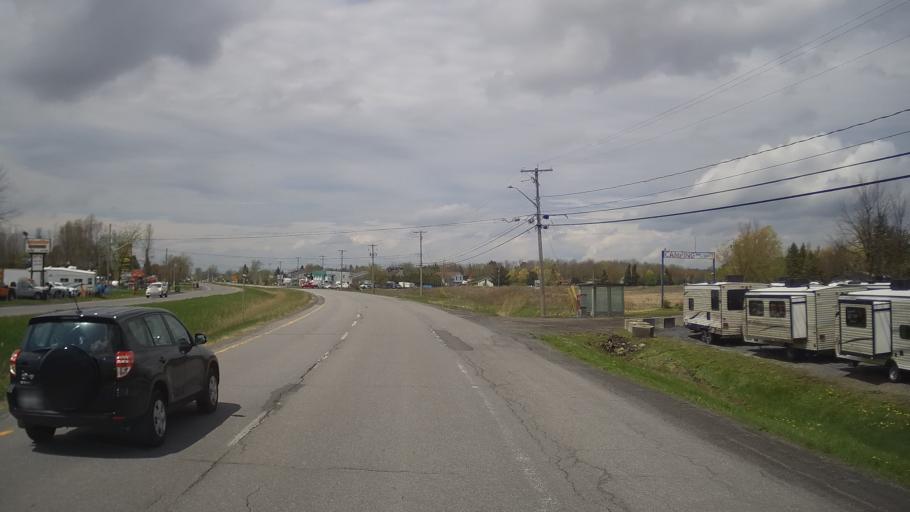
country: CA
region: Quebec
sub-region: Monteregie
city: Carignan
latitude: 45.3758
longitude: -73.3572
